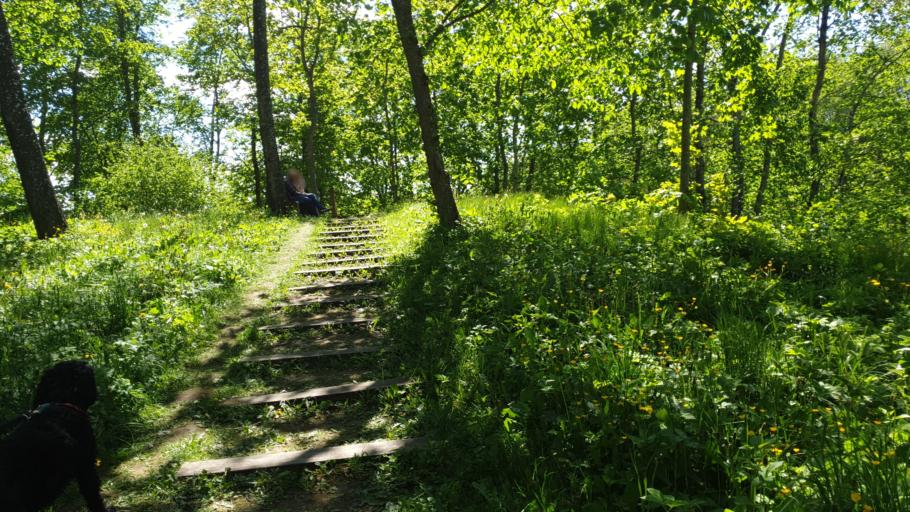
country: LT
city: Moletai
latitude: 55.0727
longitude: 25.4150
